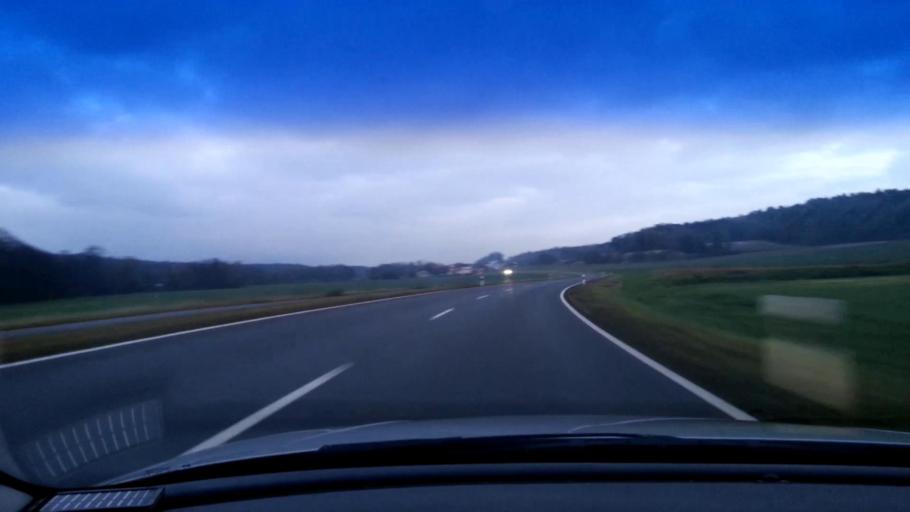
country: DE
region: Bavaria
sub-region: Upper Franconia
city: Pettstadt
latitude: 49.8463
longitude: 10.9057
